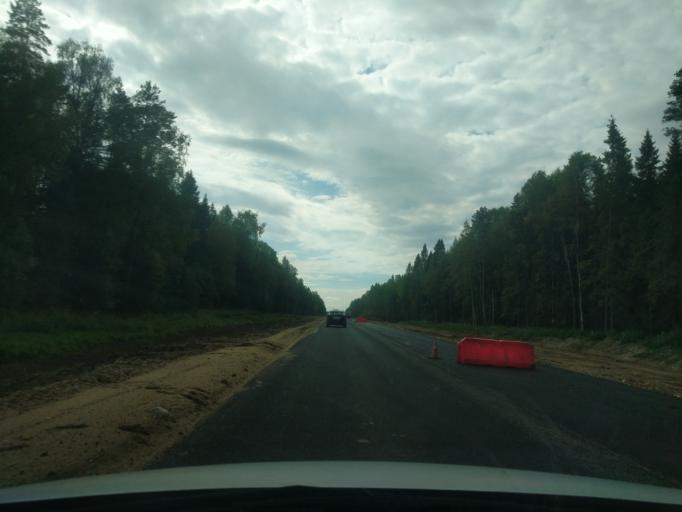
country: RU
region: Kostroma
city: Sudislavl'
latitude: 57.8449
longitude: 41.5795
